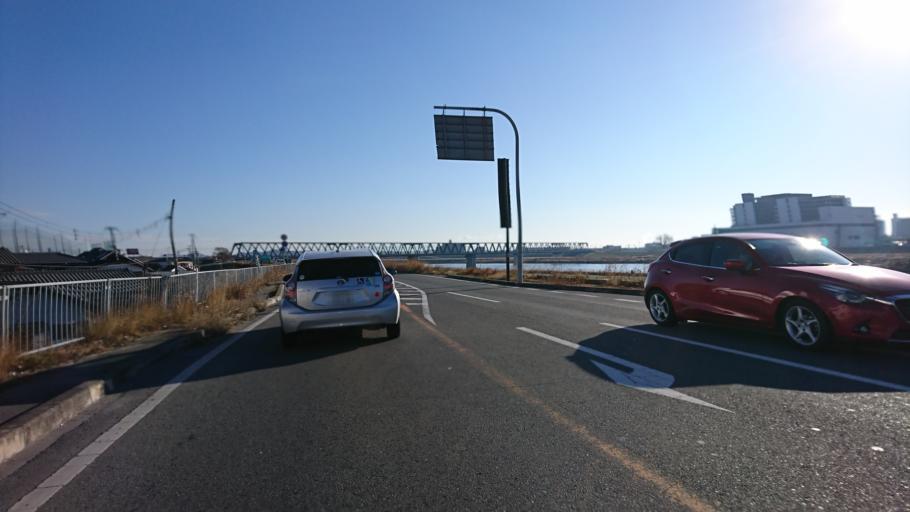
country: JP
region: Hyogo
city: Kakogawacho-honmachi
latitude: 34.7744
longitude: 134.8276
